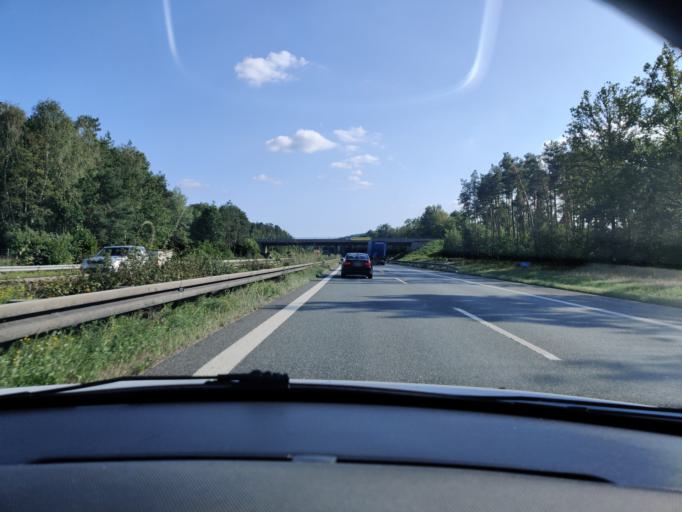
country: DE
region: Bavaria
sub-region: Upper Palatinate
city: Wackersdorf
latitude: 49.3447
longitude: 12.1499
